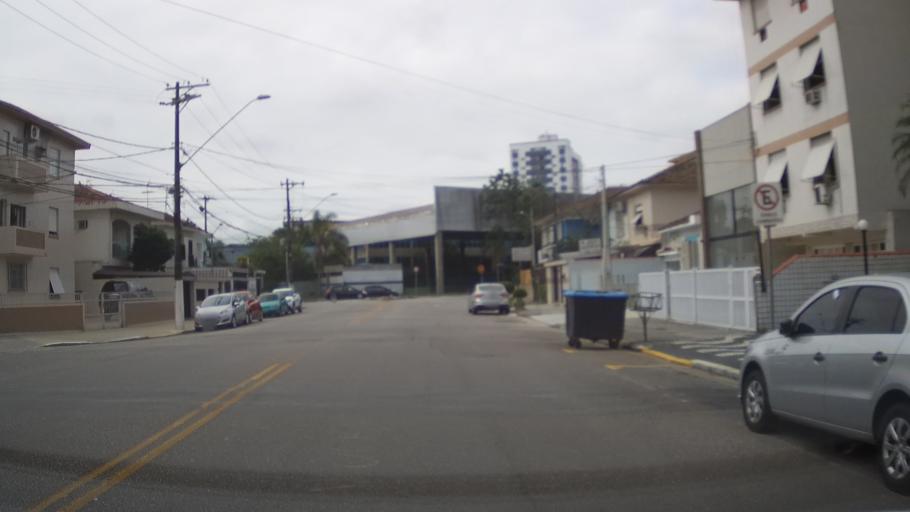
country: BR
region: Sao Paulo
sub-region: Santos
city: Santos
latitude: -23.9827
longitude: -46.3008
